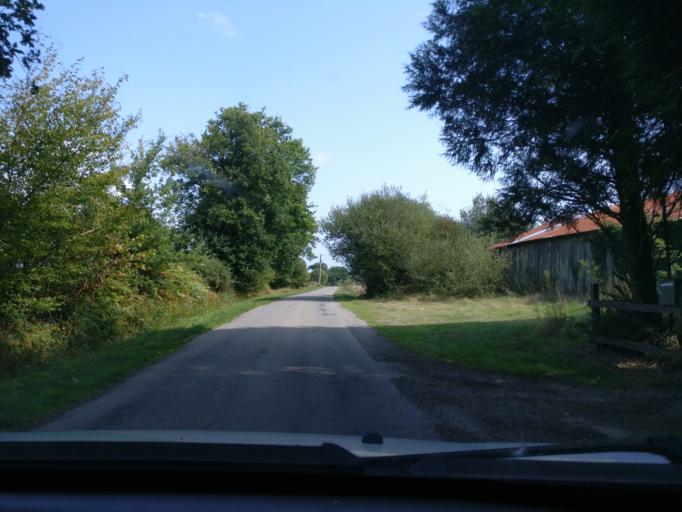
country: FR
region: Brittany
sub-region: Departement d'Ille-et-Vilaine
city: Gosne
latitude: 48.2636
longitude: -1.4810
